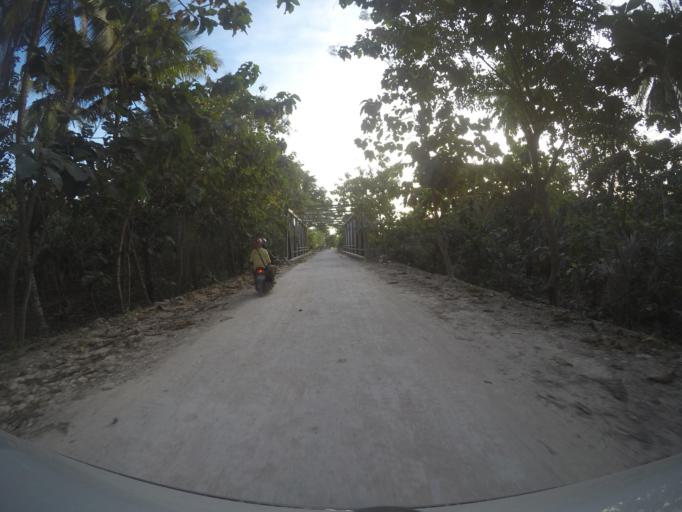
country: TL
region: Viqueque
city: Viqueque
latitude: -8.9429
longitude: 126.4513
